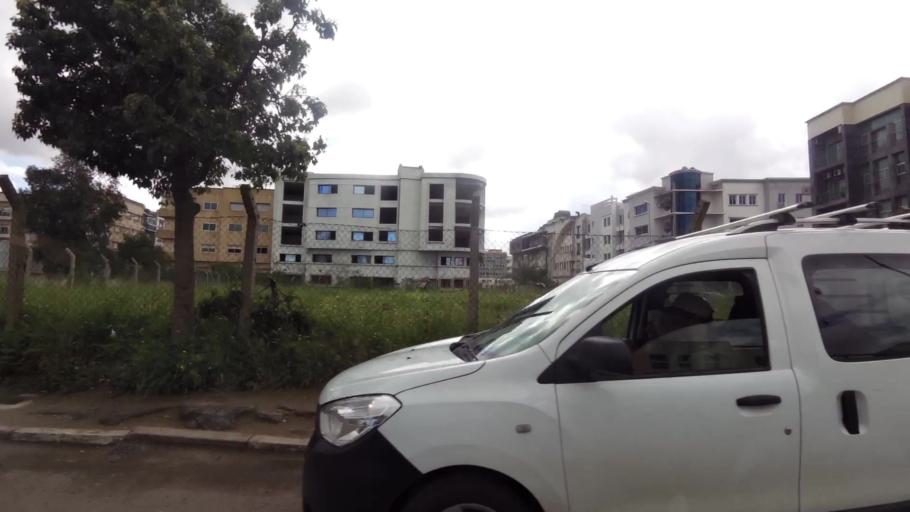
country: MA
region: Grand Casablanca
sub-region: Nouaceur
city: Bouskoura
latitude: 33.5206
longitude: -7.6522
